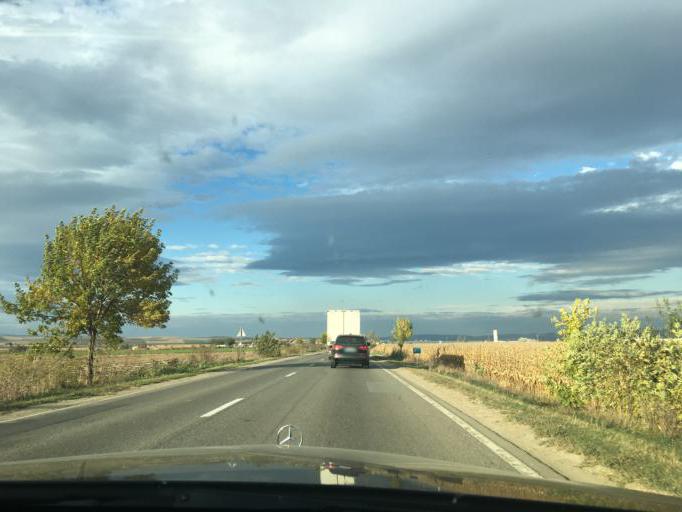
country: RO
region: Alba
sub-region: Comuna Galda de Jos
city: Galda de Jos
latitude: 46.1720
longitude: 23.6518
